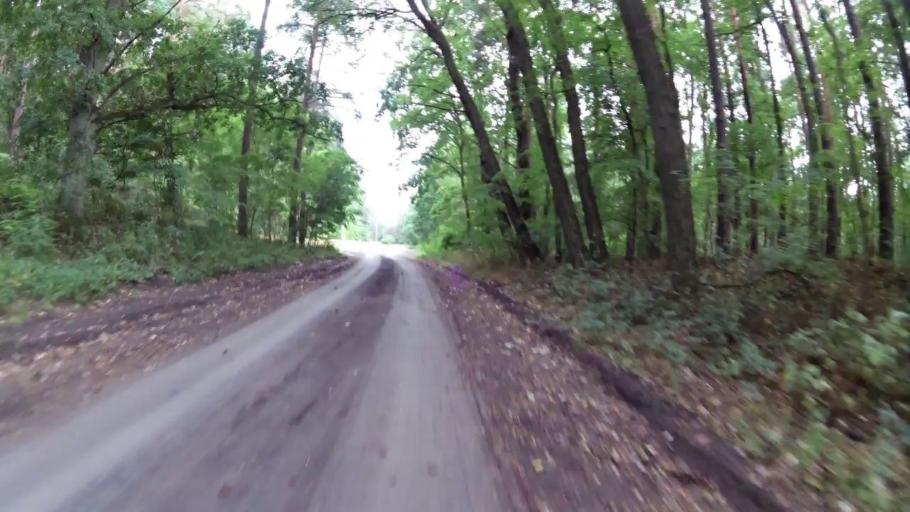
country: PL
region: West Pomeranian Voivodeship
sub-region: Powiat mysliborski
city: Debno
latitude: 52.8112
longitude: 14.7235
